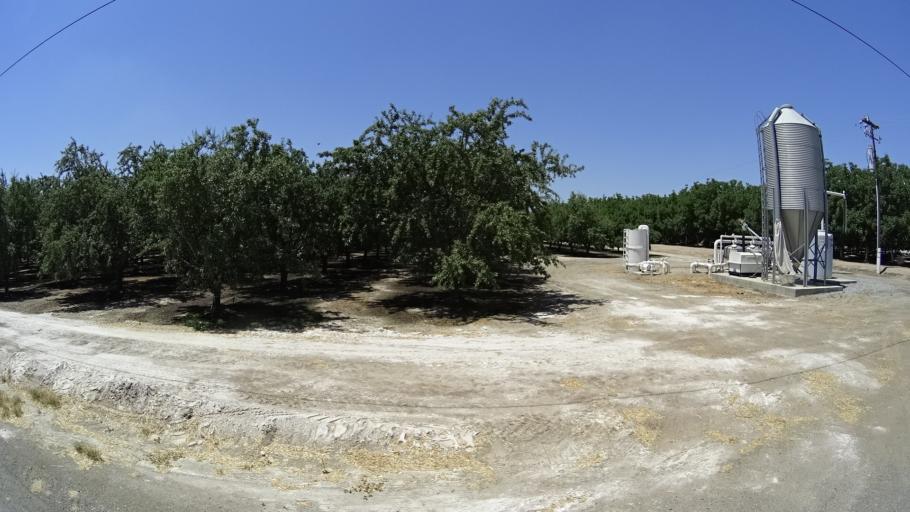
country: US
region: California
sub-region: Kings County
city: Armona
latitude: 36.3315
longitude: -119.7269
